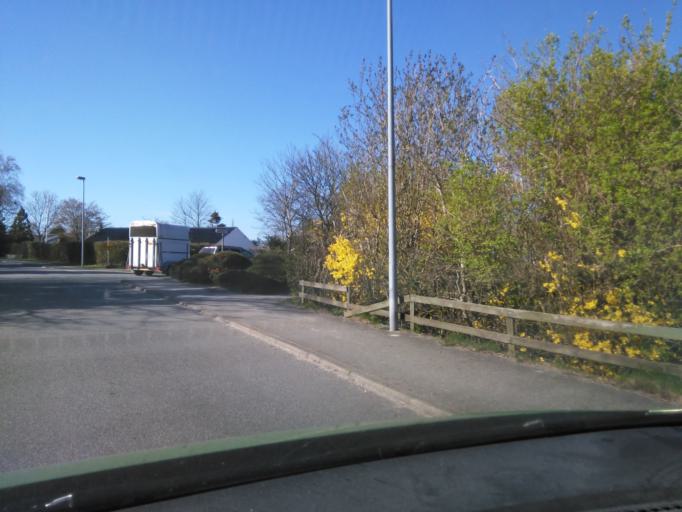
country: DK
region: South Denmark
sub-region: Varde Kommune
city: Oksbol
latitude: 55.6570
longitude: 8.2888
